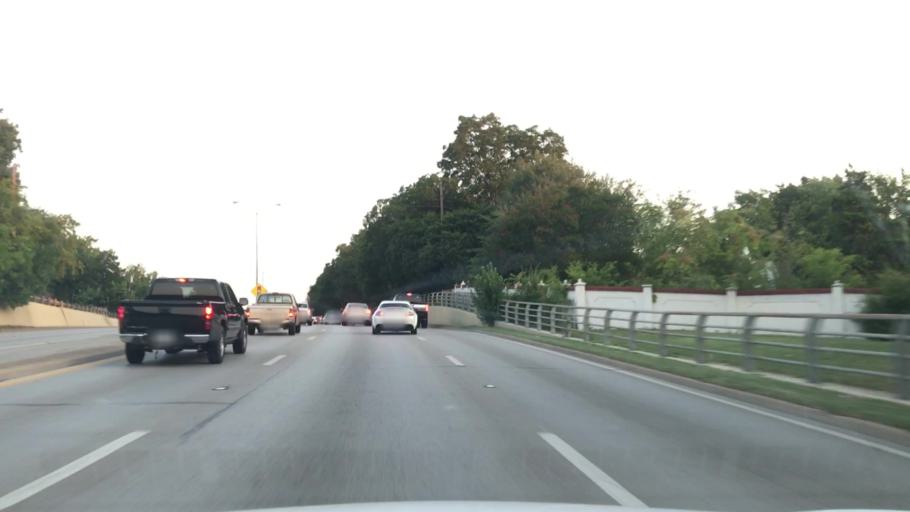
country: US
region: Texas
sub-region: Dallas County
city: Highland Park
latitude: 32.8211
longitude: -96.6923
